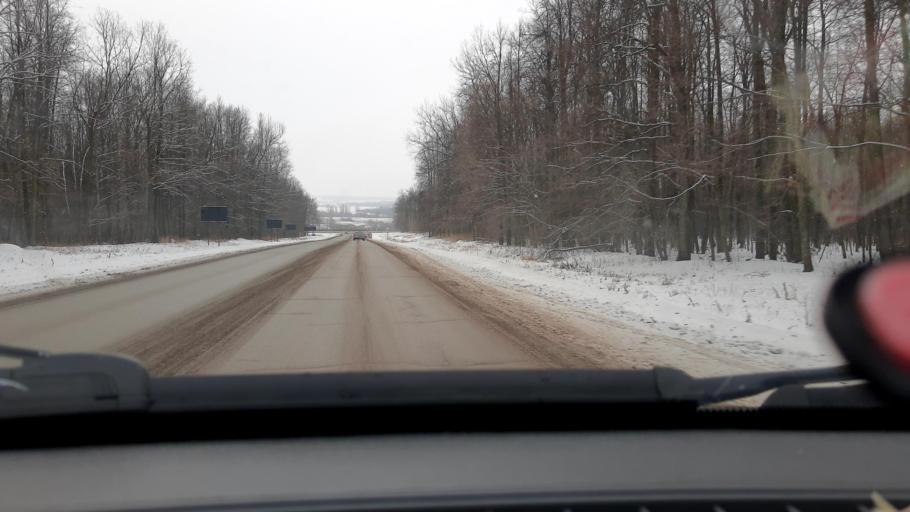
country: RU
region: Bashkortostan
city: Iglino
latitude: 54.7675
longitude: 56.4135
